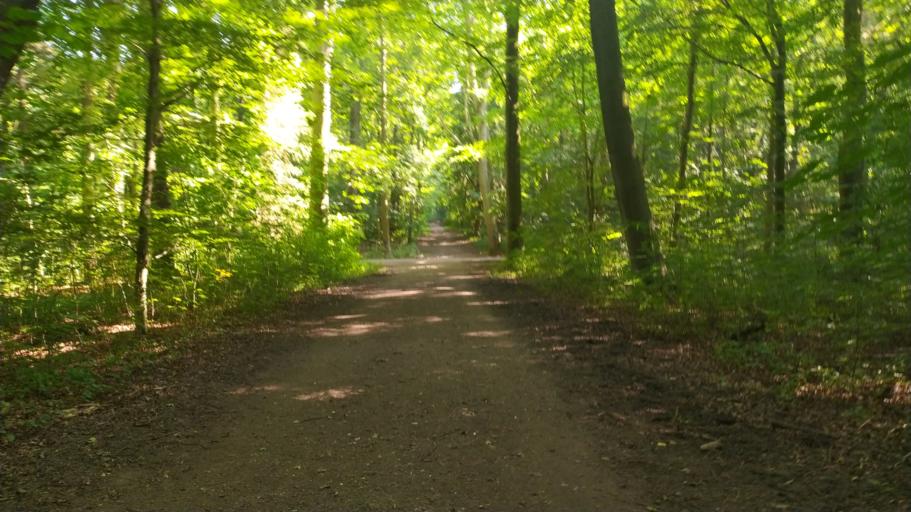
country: DE
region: Schleswig-Holstein
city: Kronshagen
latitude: 54.3658
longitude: 10.1013
